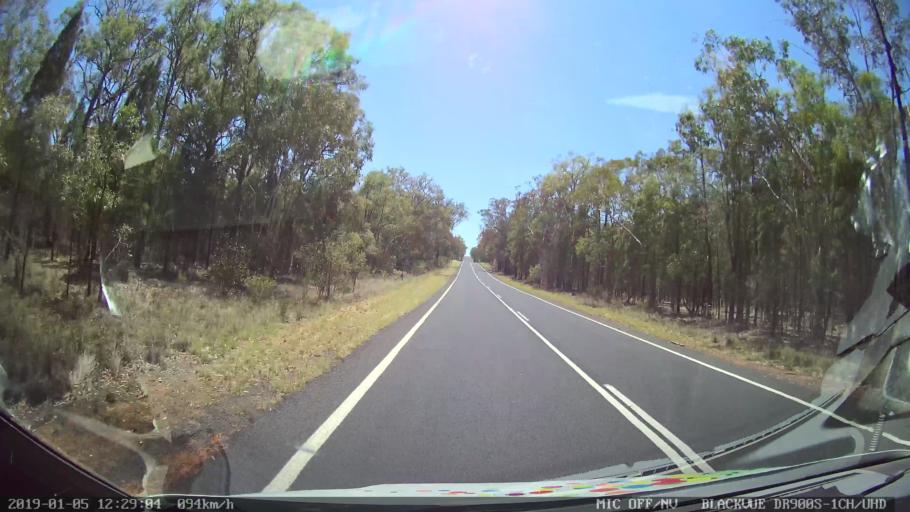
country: AU
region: New South Wales
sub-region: Warrumbungle Shire
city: Coonabarabran
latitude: -31.2358
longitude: 149.3322
